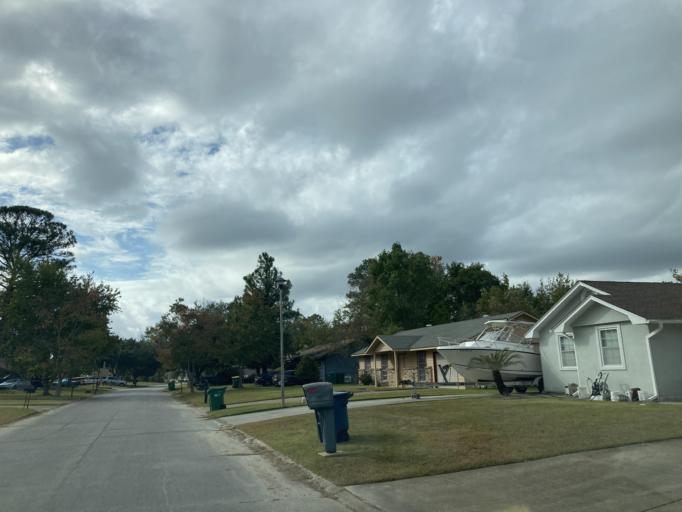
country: US
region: Mississippi
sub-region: Jackson County
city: Gulf Hills
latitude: 30.4359
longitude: -88.8184
